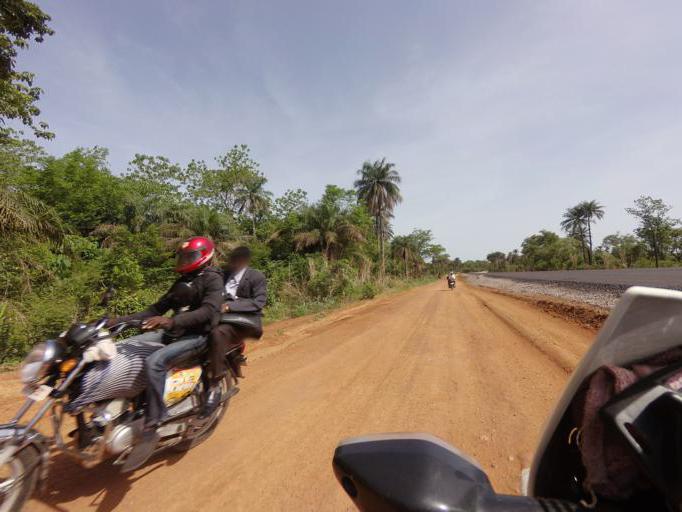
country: SL
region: Northern Province
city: Makeni
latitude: 9.0566
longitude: -12.1760
